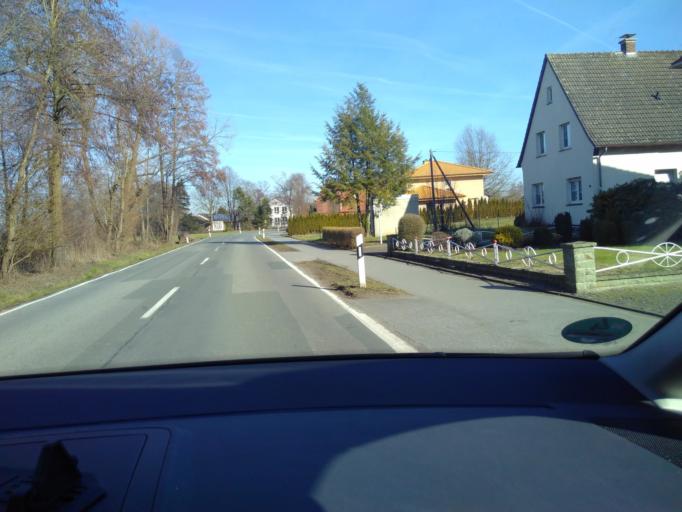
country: DE
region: North Rhine-Westphalia
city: Rietberg
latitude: 51.8410
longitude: 8.4502
